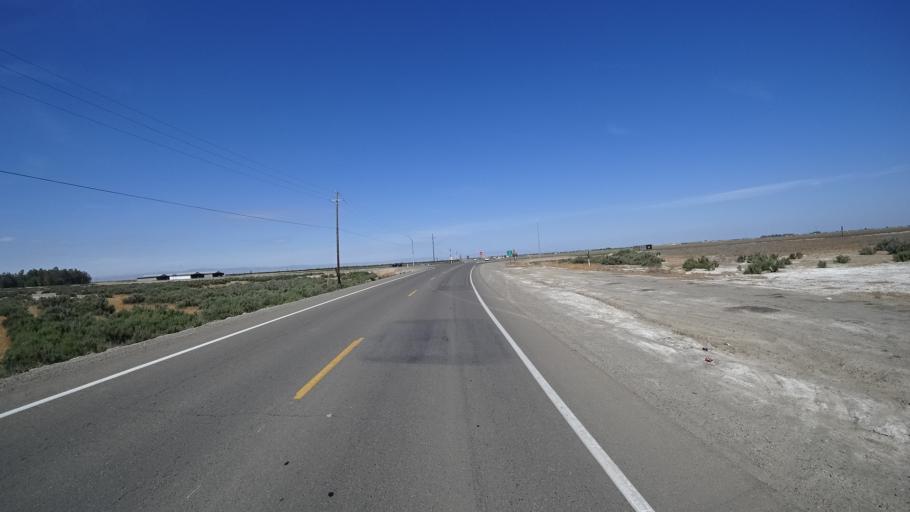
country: US
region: California
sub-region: Kings County
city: Lemoore
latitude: 36.2547
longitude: -119.8073
